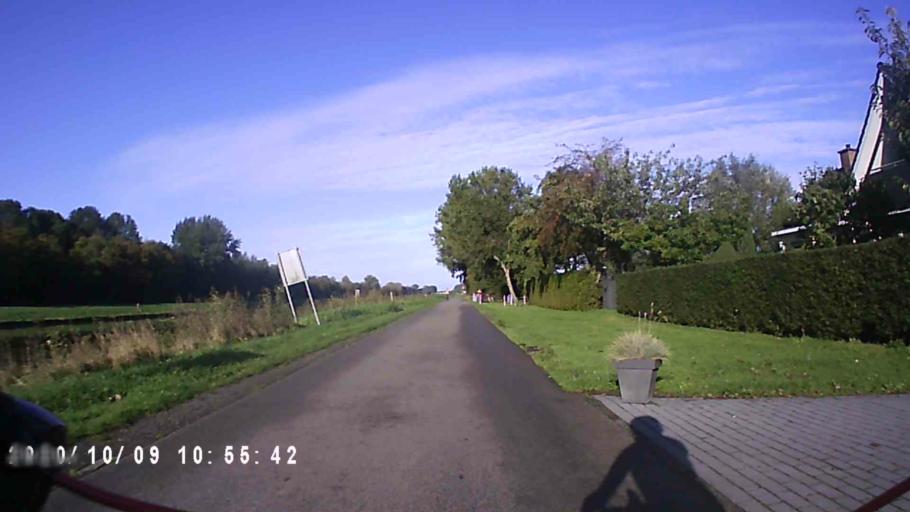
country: NL
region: Groningen
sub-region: Gemeente Groningen
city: Korrewegwijk
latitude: 53.2507
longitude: 6.5311
